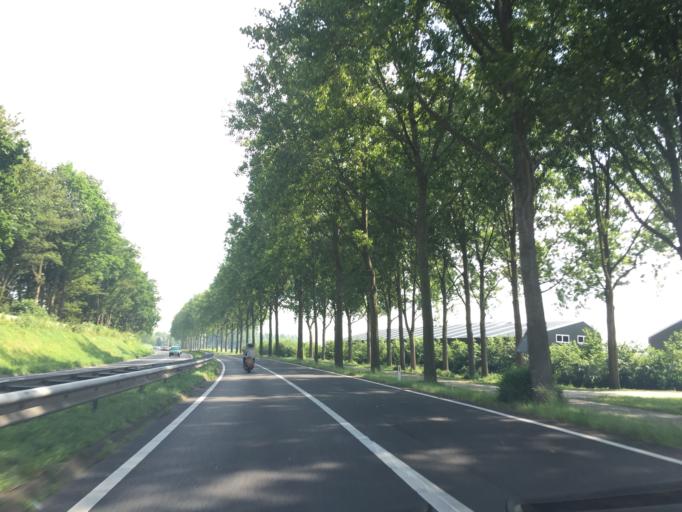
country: NL
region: South Holland
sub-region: Gemeente Leiden
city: Leiden
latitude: 52.1175
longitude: 4.4917
